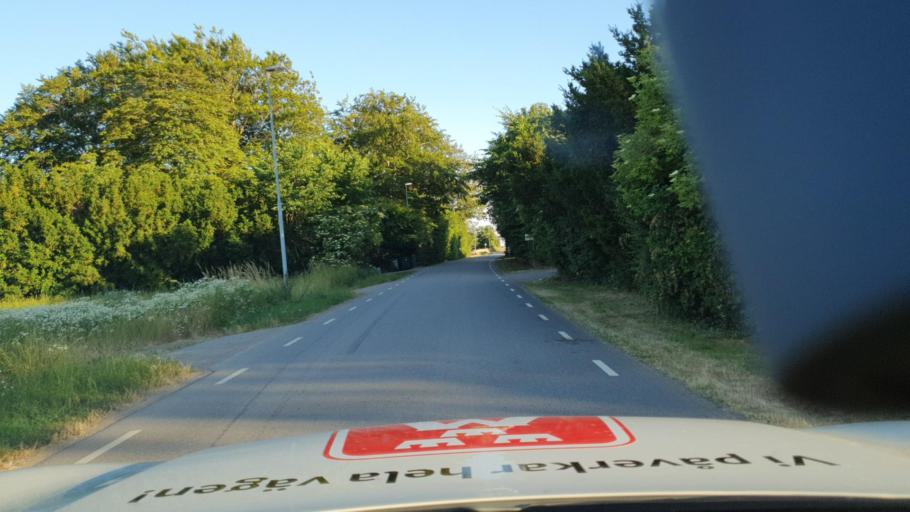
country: SE
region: Skane
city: Bjarred
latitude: 55.7174
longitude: 13.0601
